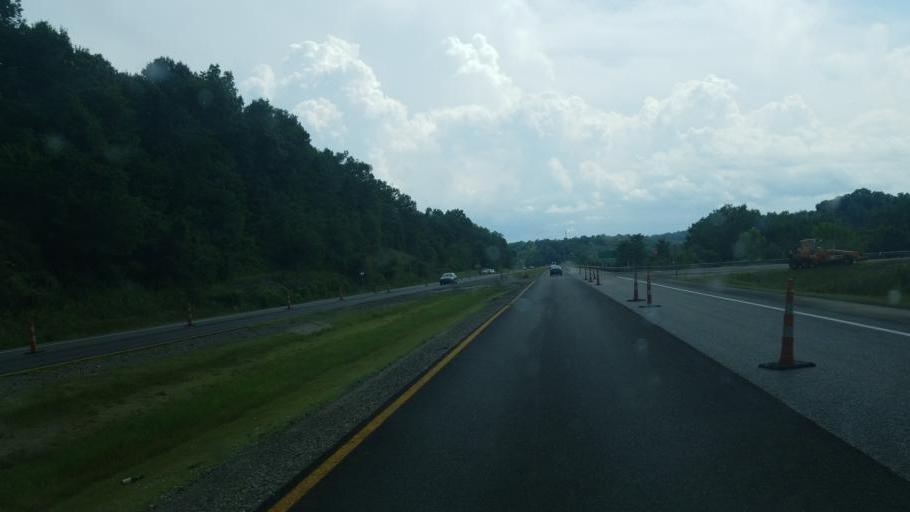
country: US
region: West Virginia
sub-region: Kanawha County
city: Alum Creek
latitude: 38.2438
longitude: -81.8377
